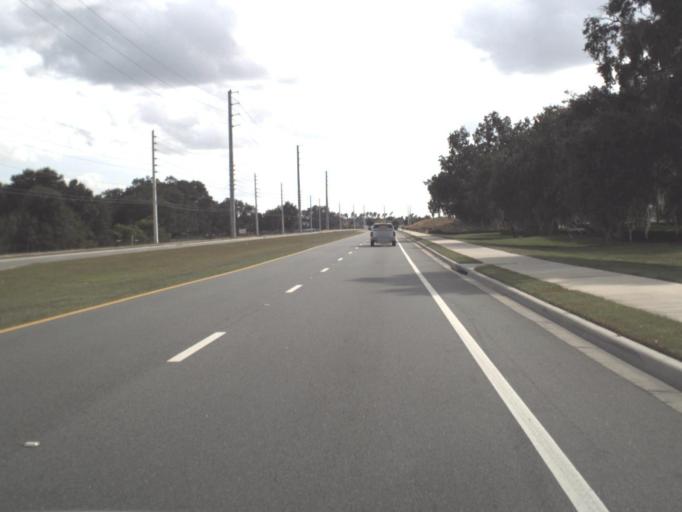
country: US
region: Florida
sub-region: Osceola County
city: Saint Cloud
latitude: 28.2593
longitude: -81.2418
